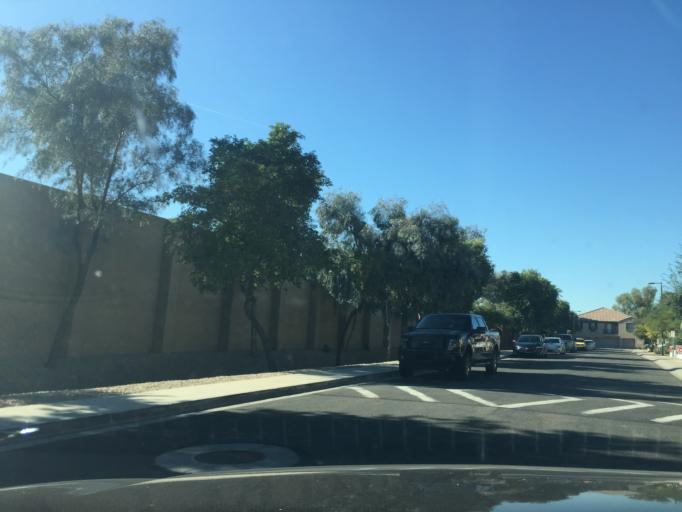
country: US
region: Arizona
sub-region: Maricopa County
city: Tolleson
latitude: 33.4636
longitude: -112.2307
